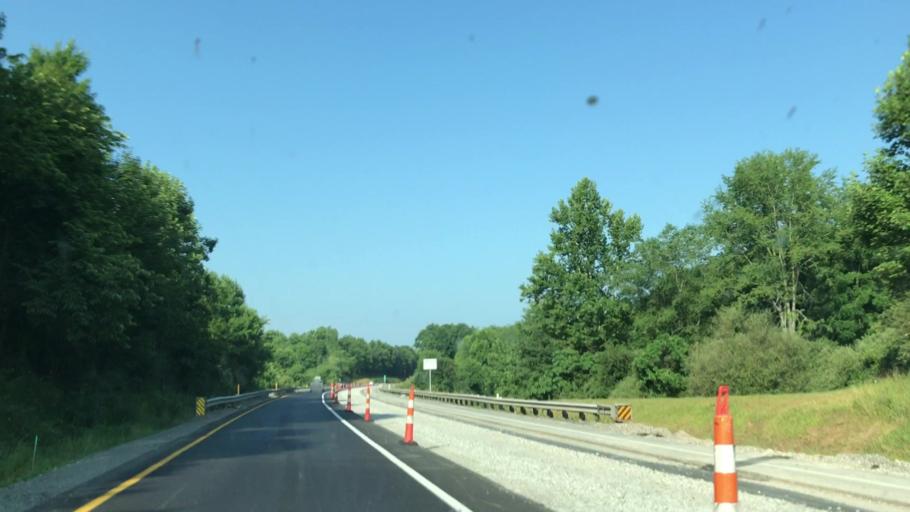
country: US
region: West Virginia
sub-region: Braxton County
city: Sutton
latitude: 38.6925
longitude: -80.6763
